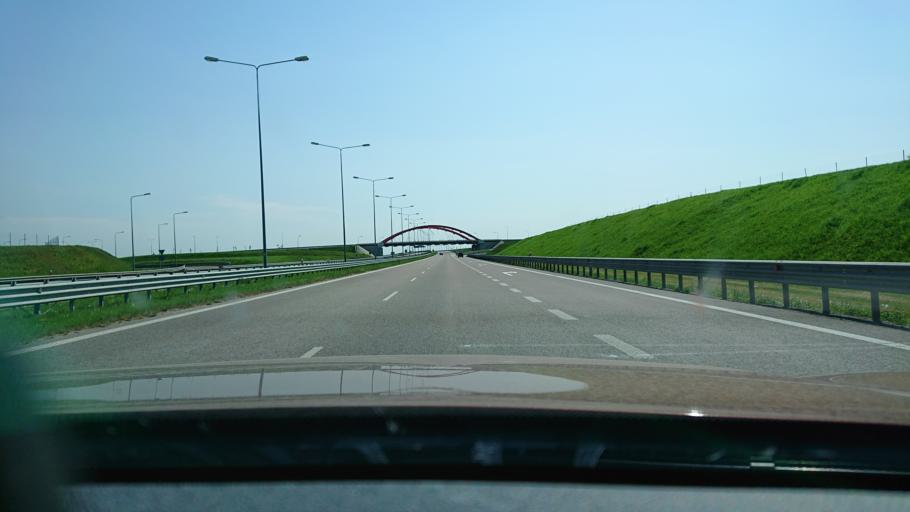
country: PL
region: Subcarpathian Voivodeship
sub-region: Powiat jaroslawski
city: Radymno
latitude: 49.9123
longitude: 22.8043
